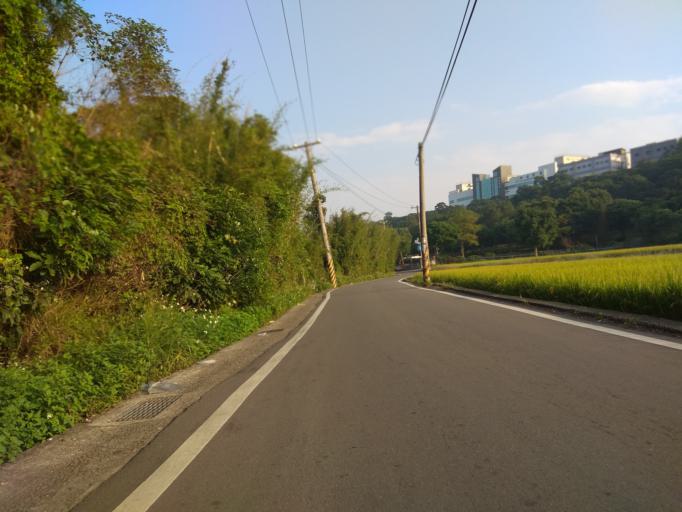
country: TW
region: Taiwan
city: Daxi
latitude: 24.9084
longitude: 121.1967
